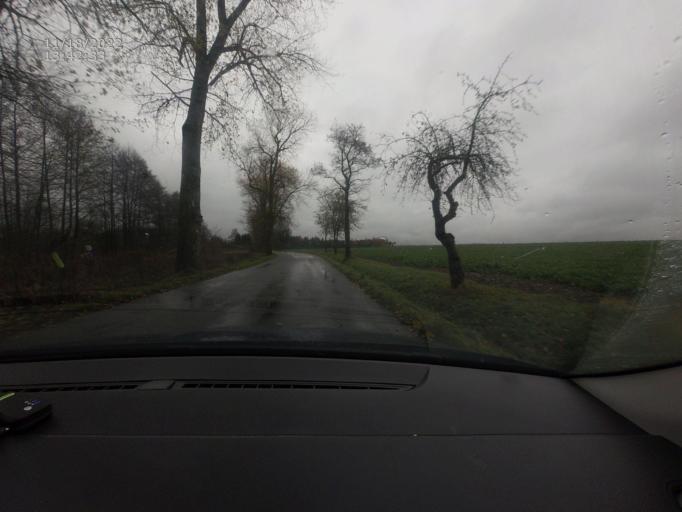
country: CZ
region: Plzensky
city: Kasejovice
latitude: 49.4354
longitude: 13.7994
